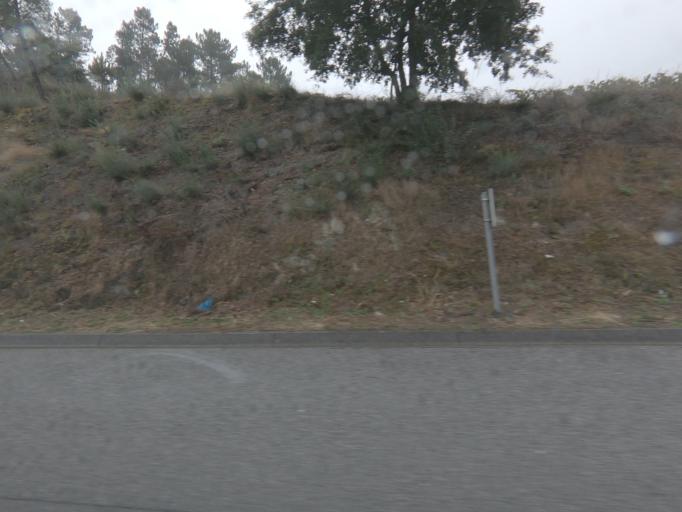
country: PT
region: Porto
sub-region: Lousada
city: Meinedo
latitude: 41.2290
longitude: -8.2268
